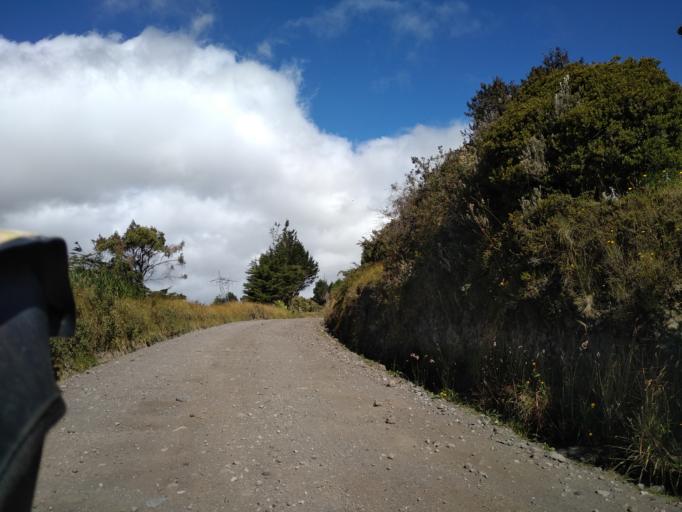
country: EC
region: Pichincha
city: Machachi
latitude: -0.5352
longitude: -78.4781
